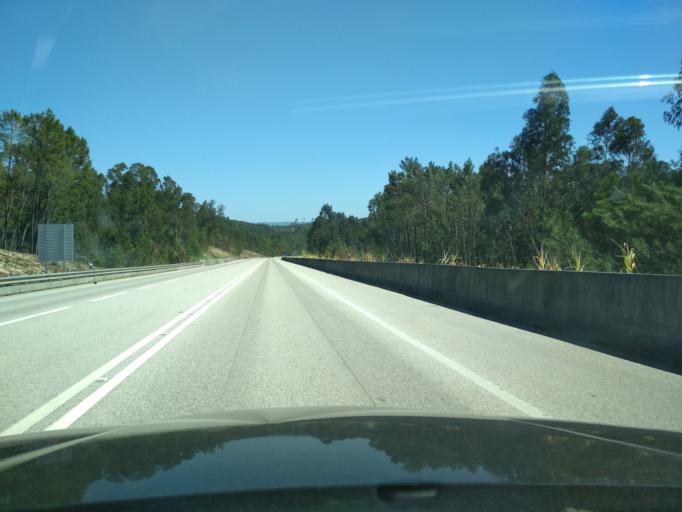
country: PT
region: Leiria
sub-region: Pombal
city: Lourical
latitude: 39.9883
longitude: -8.7748
